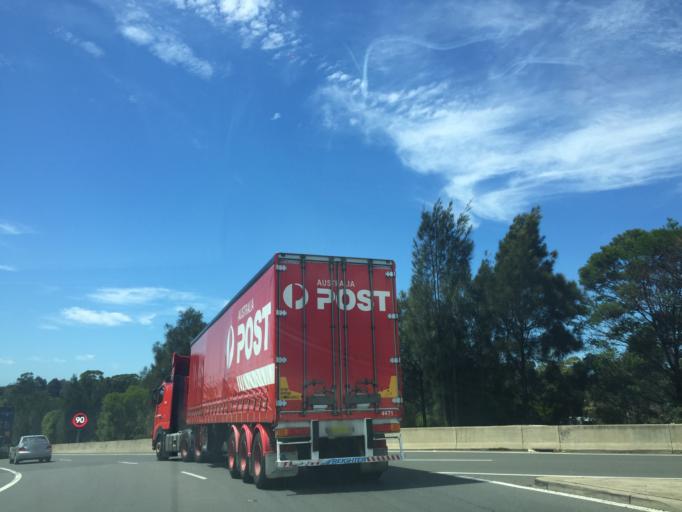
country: AU
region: New South Wales
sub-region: Canterbury
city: Roselands
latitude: -33.9428
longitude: 151.0771
